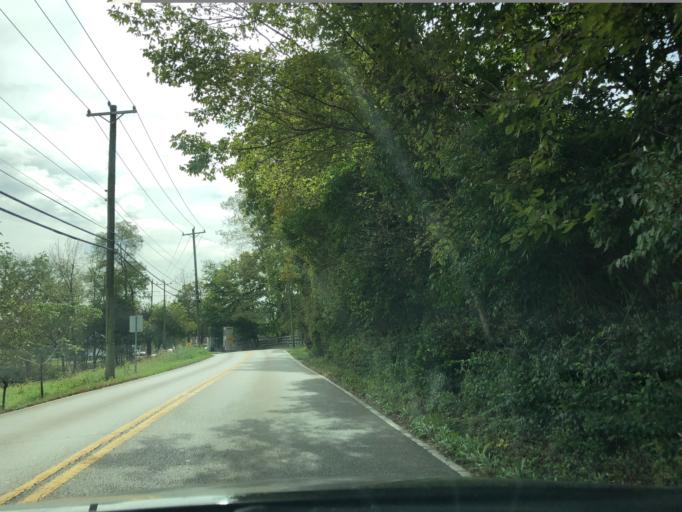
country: US
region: Ohio
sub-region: Hamilton County
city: The Village of Indian Hill
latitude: 39.2151
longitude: -84.2986
